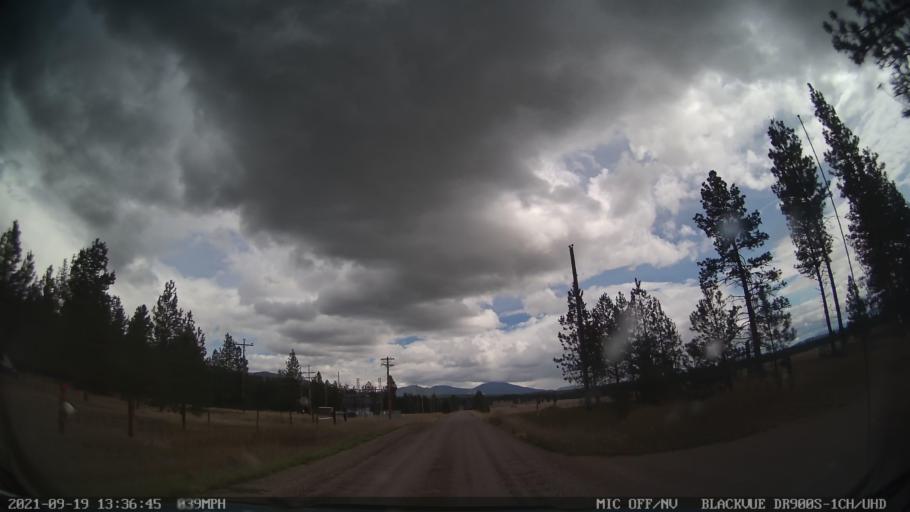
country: US
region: Montana
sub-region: Missoula County
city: Seeley Lake
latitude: 47.1066
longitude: -113.2935
